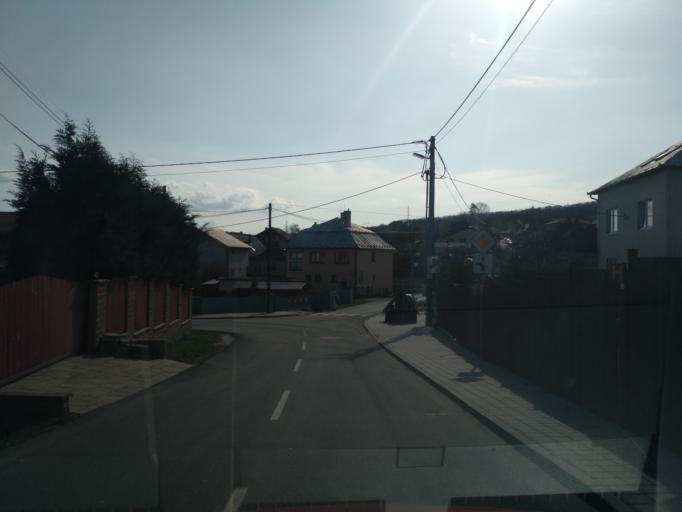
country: SK
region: Kosicky
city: Kosice
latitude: 48.6911
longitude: 21.1921
